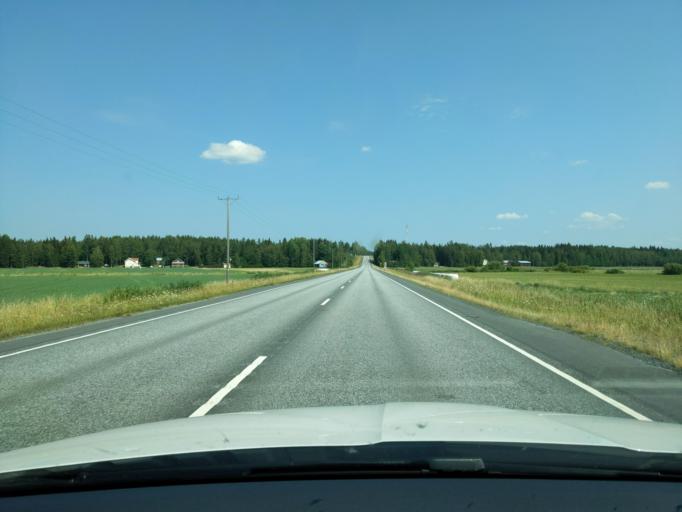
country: FI
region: Haeme
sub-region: Forssa
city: Ypaejae
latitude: 60.7613
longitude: 23.3147
